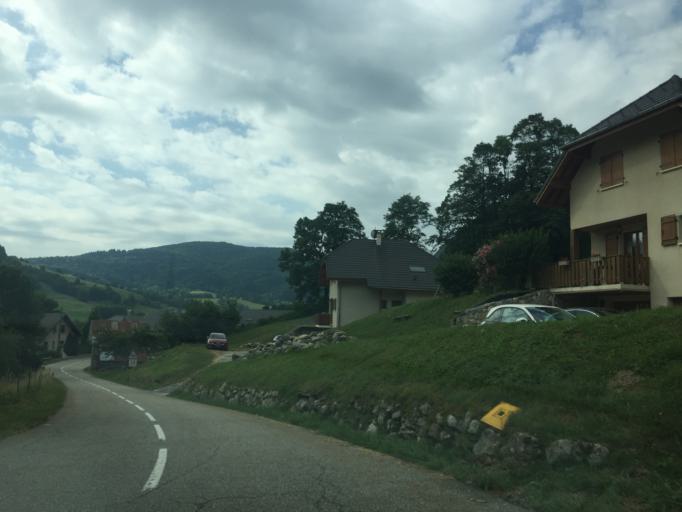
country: FR
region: Rhone-Alpes
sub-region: Departement de la Savoie
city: Montmelian
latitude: 45.5448
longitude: 6.0347
